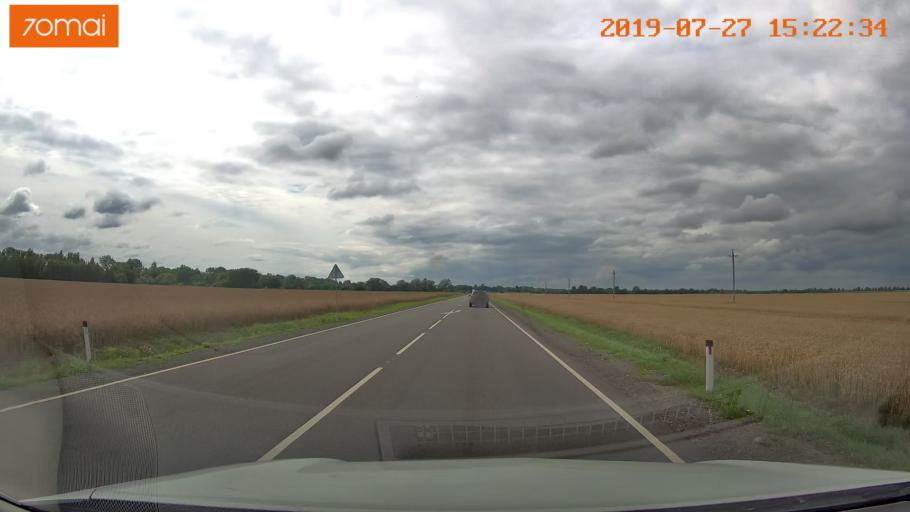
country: RU
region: Kaliningrad
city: Nesterov
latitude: 54.6339
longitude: 22.6554
